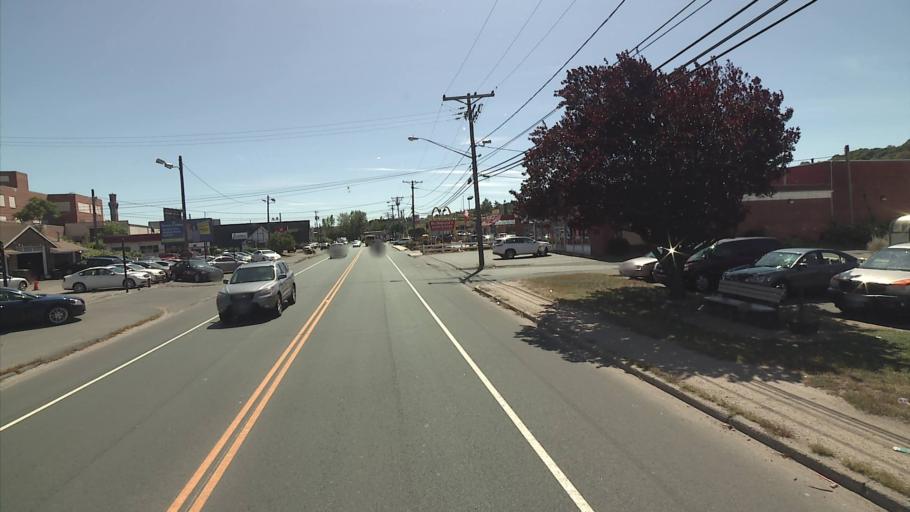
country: US
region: Connecticut
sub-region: New Haven County
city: Waterbury
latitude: 41.5596
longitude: -73.0529
